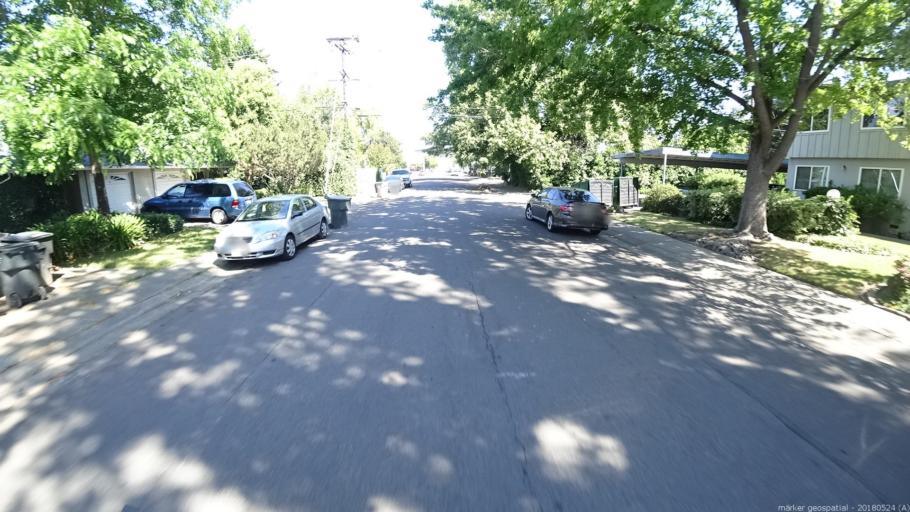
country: US
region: California
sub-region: Sacramento County
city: Sacramento
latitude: 38.6015
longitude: -121.4647
